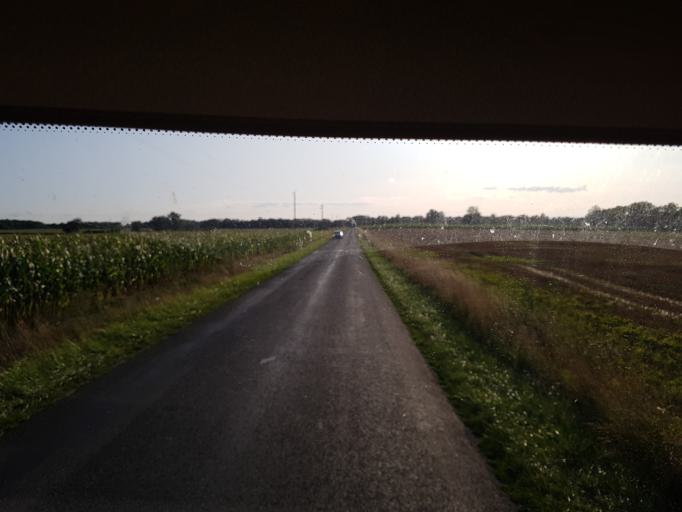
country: FR
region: Rhone-Alpes
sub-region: Departement de l'Ain
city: Villars-les-Dombes
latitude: 45.9686
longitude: 5.0809
